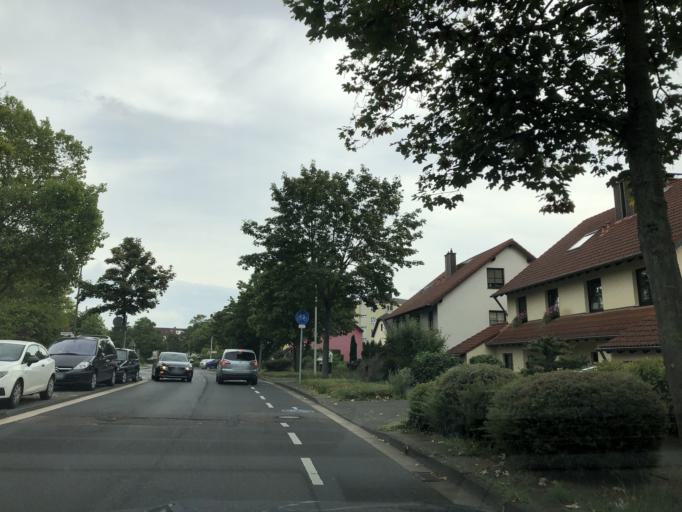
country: DE
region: North Rhine-Westphalia
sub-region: Regierungsbezirk Koln
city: Bonn
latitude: 50.7318
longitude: 7.1287
